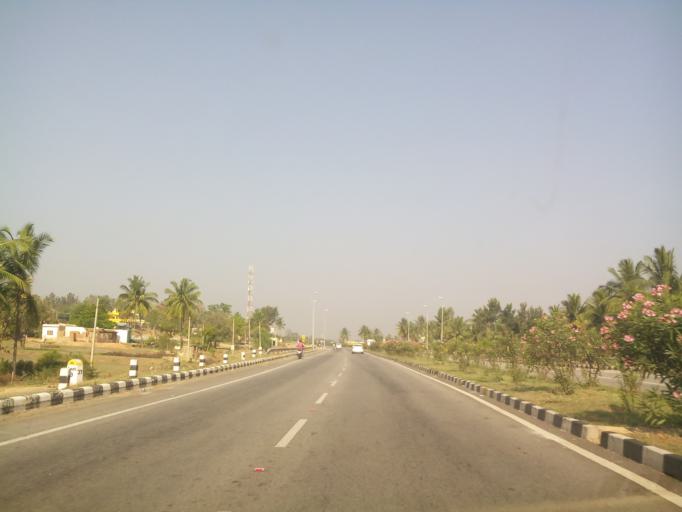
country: IN
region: Karnataka
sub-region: Bangalore Rural
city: Nelamangala
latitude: 13.0661
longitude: 77.3229
